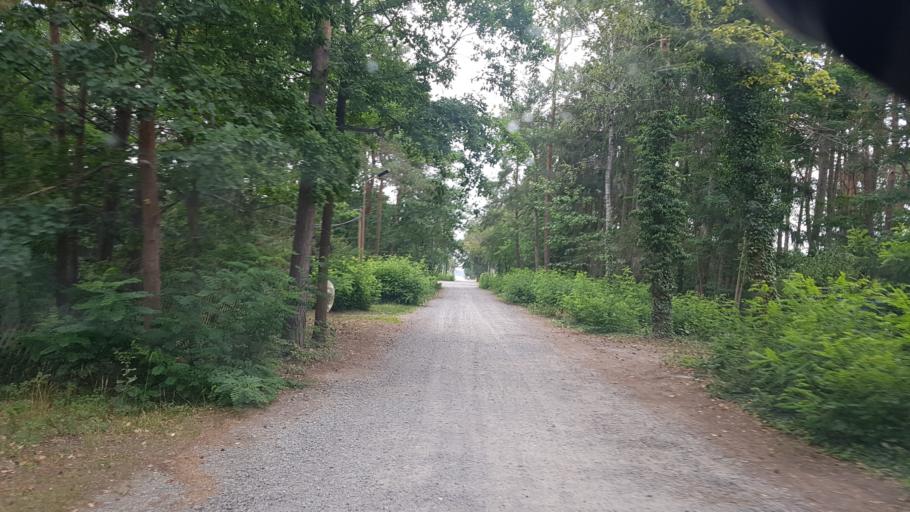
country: DE
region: Brandenburg
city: Gross Koris
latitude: 52.1621
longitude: 13.6934
